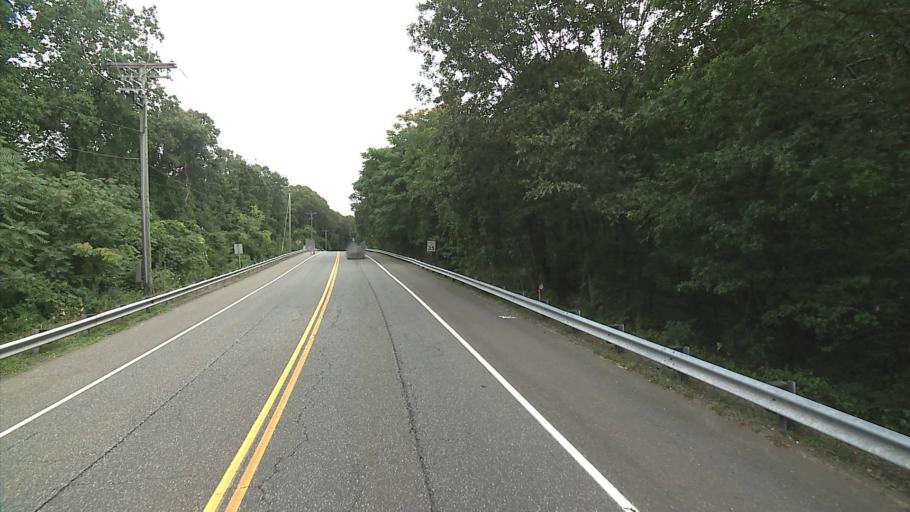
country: US
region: Connecticut
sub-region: New London County
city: Niantic
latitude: 41.2933
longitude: -72.2659
